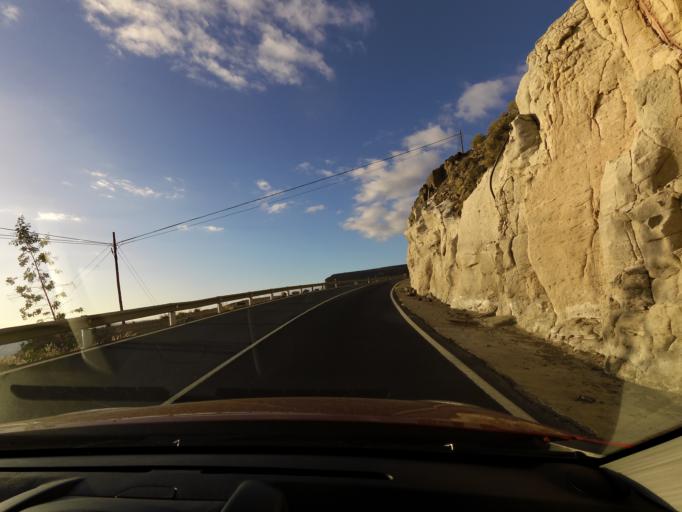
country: ES
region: Canary Islands
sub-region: Provincia de Las Palmas
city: Puerto Rico
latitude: 27.7983
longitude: -15.7358
